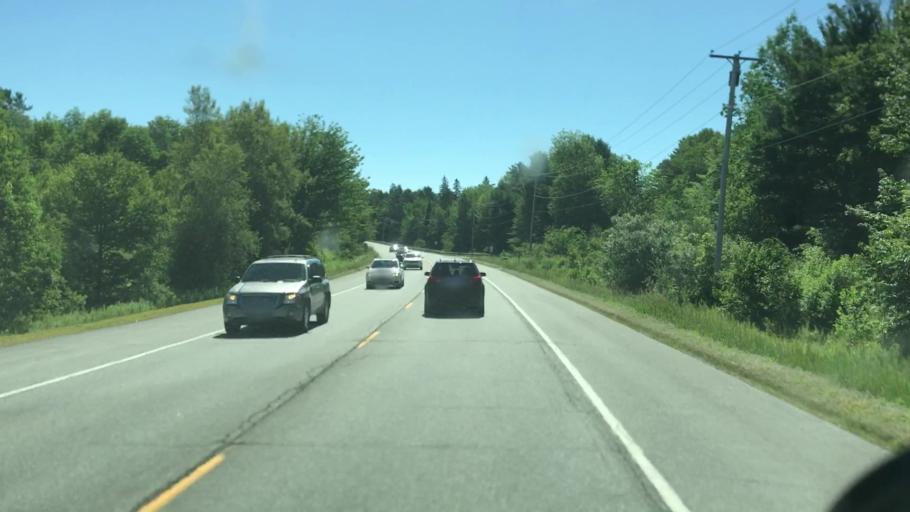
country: US
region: Maine
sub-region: Penobscot County
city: Holden
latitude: 44.7553
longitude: -68.6836
